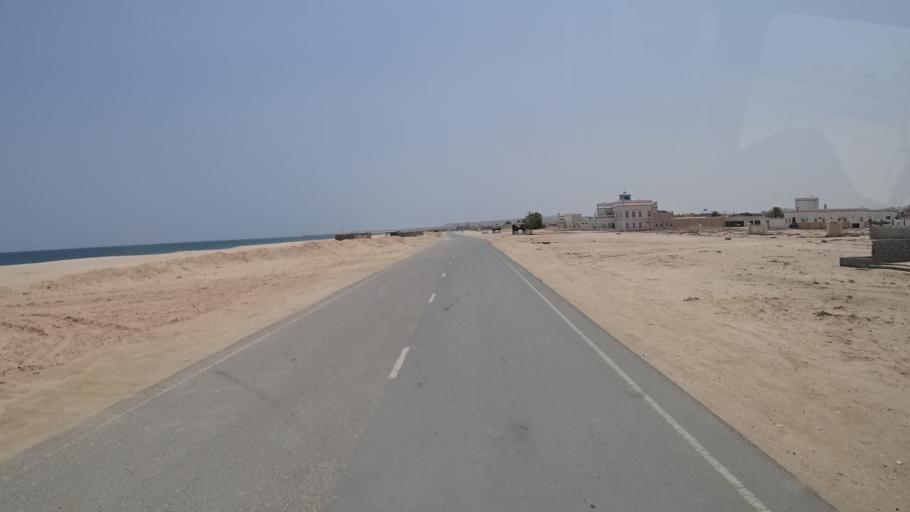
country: OM
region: Ash Sharqiyah
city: Sur
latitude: 22.5266
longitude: 59.7975
